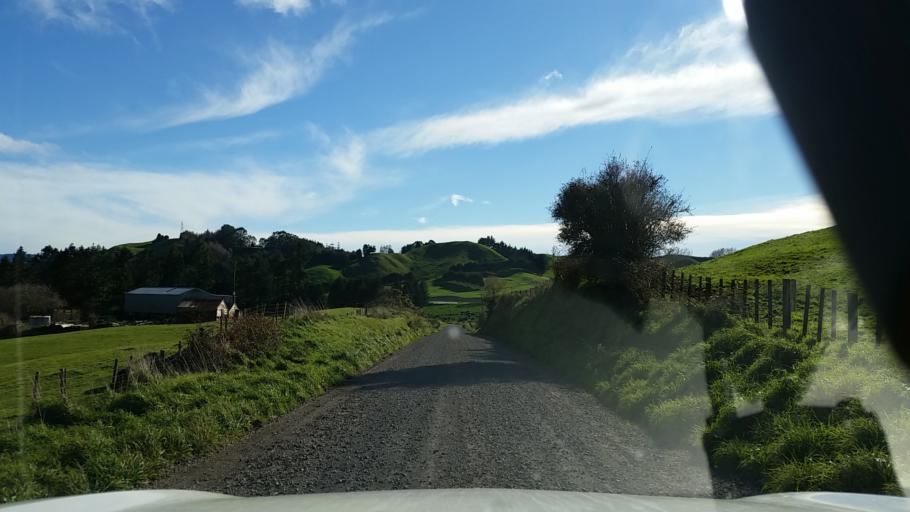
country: NZ
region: Bay of Plenty
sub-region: Rotorua District
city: Rotorua
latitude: -38.3562
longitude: 176.2323
